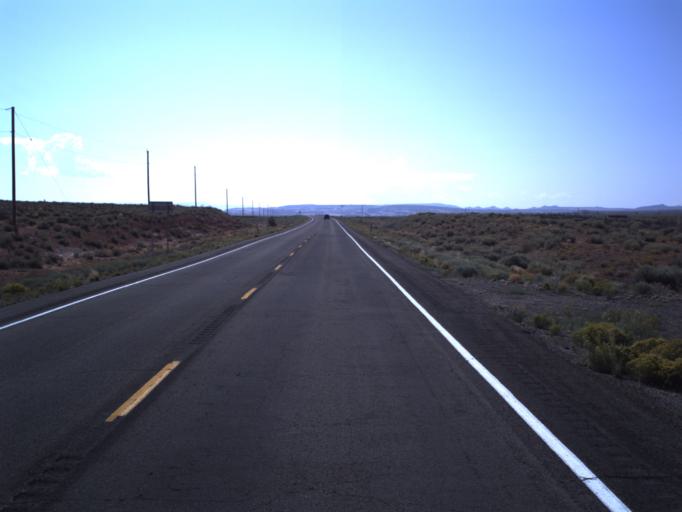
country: US
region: Utah
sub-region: San Juan County
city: Blanding
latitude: 37.1529
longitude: -109.5677
